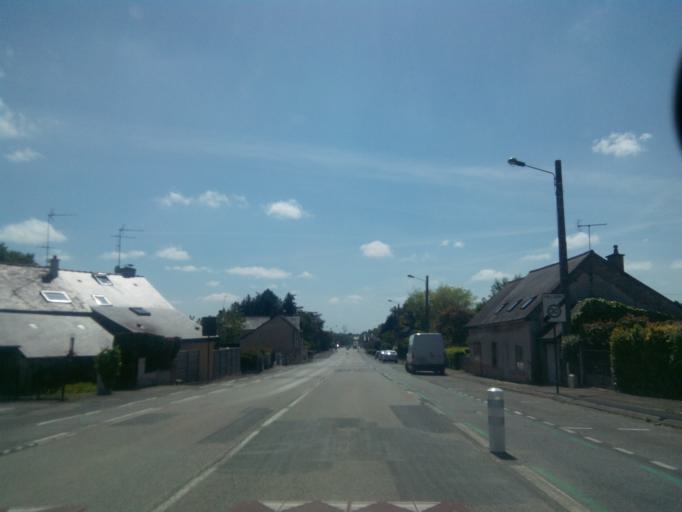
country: FR
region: Brittany
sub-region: Departement d'Ille-et-Vilaine
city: Fouillard
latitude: 48.1584
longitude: -1.5892
